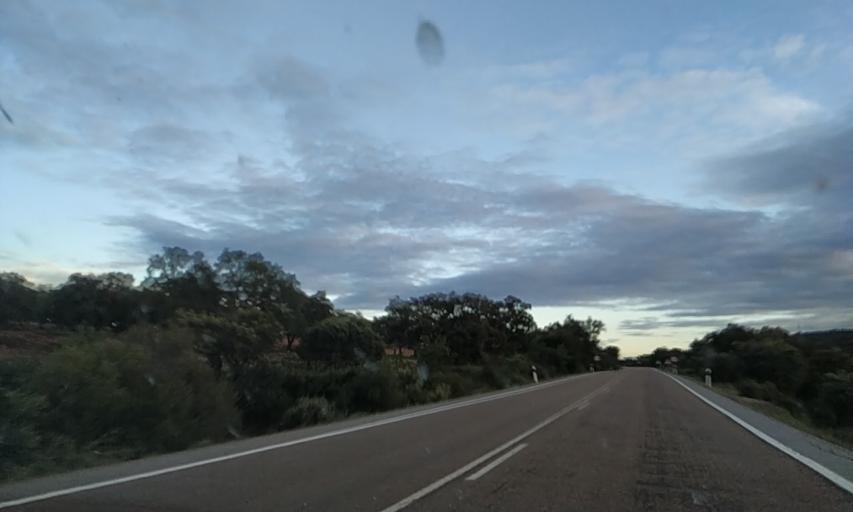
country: ES
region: Extremadura
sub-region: Provincia de Badajoz
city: Puebla de Obando
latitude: 39.2847
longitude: -6.5220
